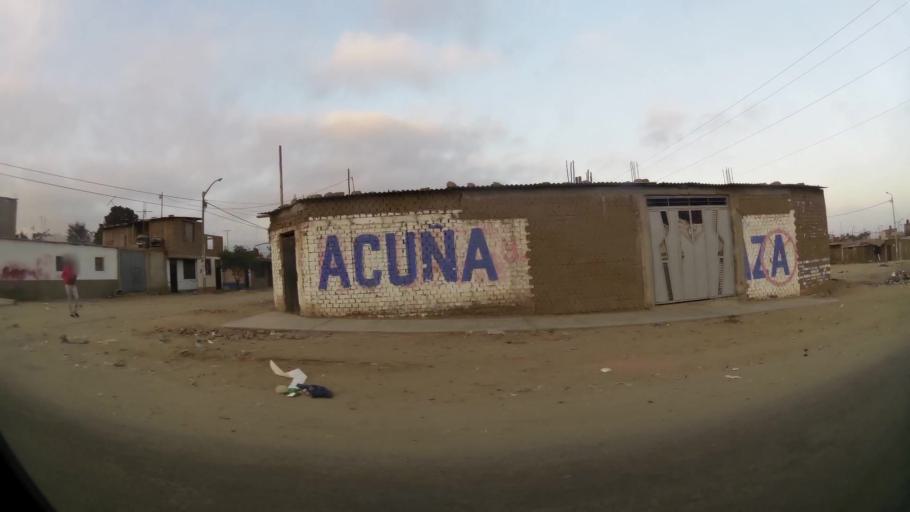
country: PE
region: La Libertad
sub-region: Provincia de Trujillo
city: El Porvenir
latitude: -8.0694
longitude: -79.0060
